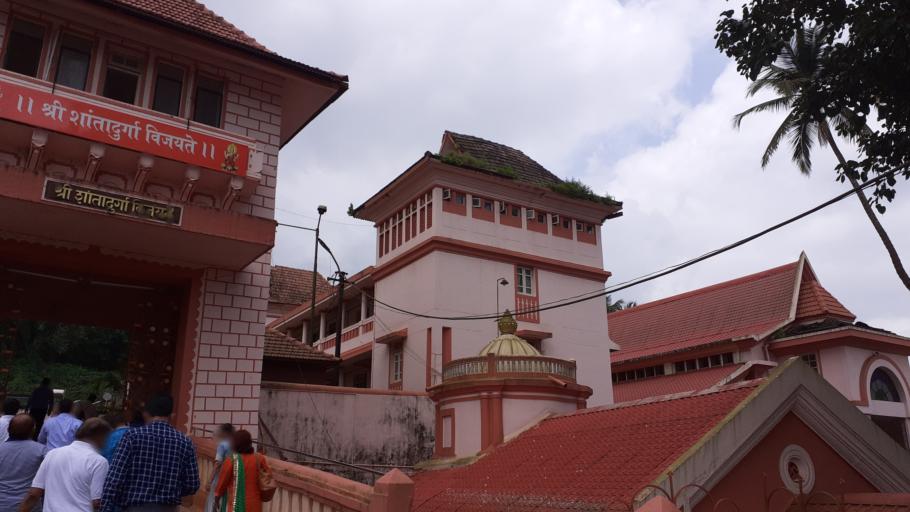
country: IN
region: Goa
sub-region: North Goa
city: Queula
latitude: 15.3964
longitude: 73.9859
